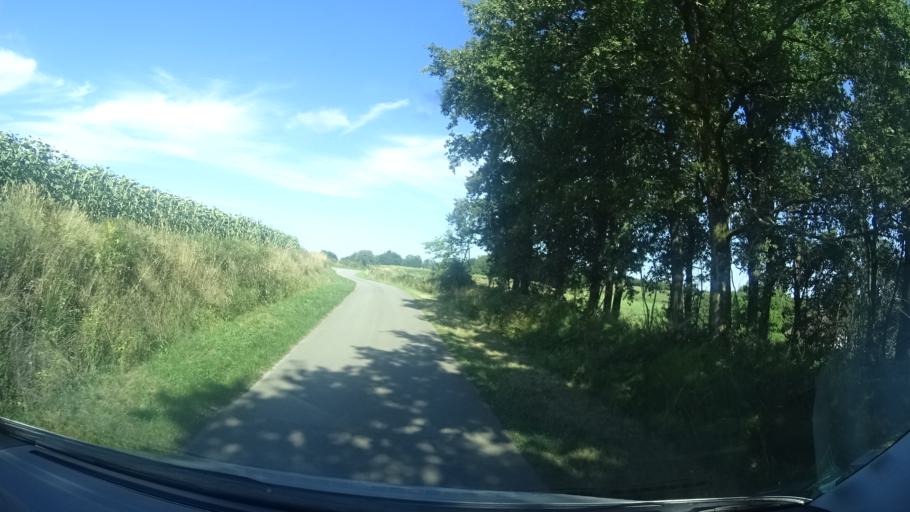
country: FR
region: Aquitaine
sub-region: Departement des Pyrenees-Atlantiques
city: Orthez
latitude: 43.5076
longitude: -0.6955
